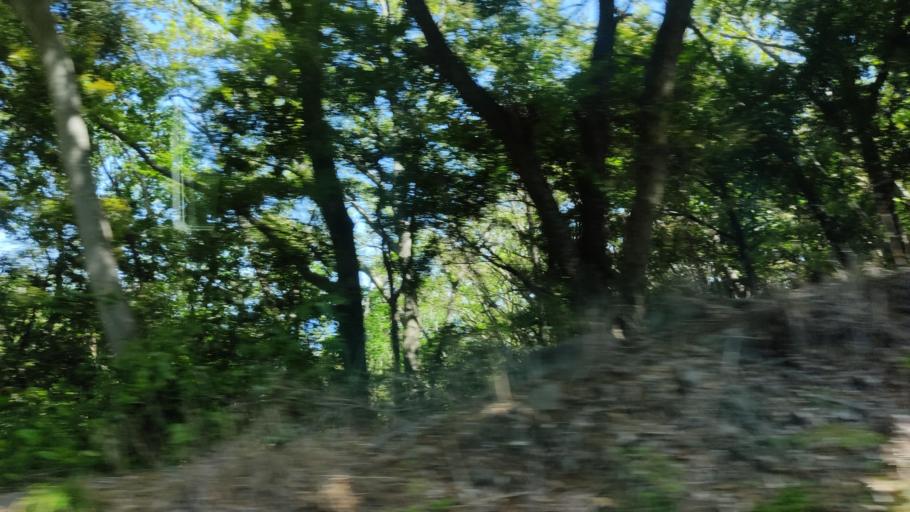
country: JP
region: Shizuoka
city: Ito
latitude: 34.9503
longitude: 139.1288
